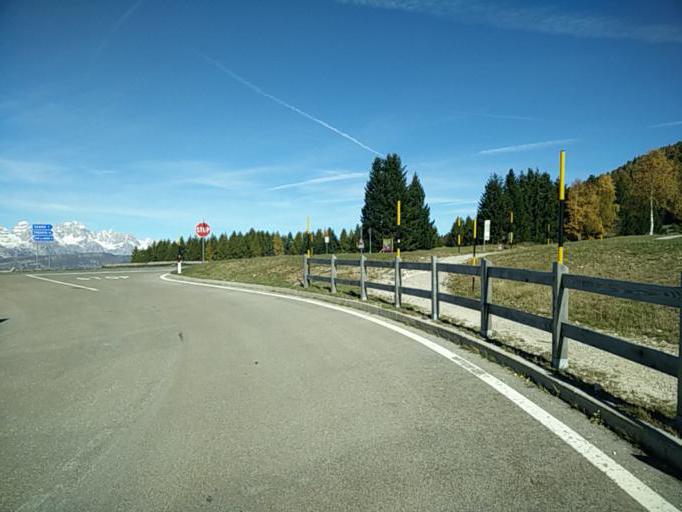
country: IT
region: Trentino-Alto Adige
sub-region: Provincia di Trento
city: Cimoneri
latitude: 46.0214
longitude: 11.0428
